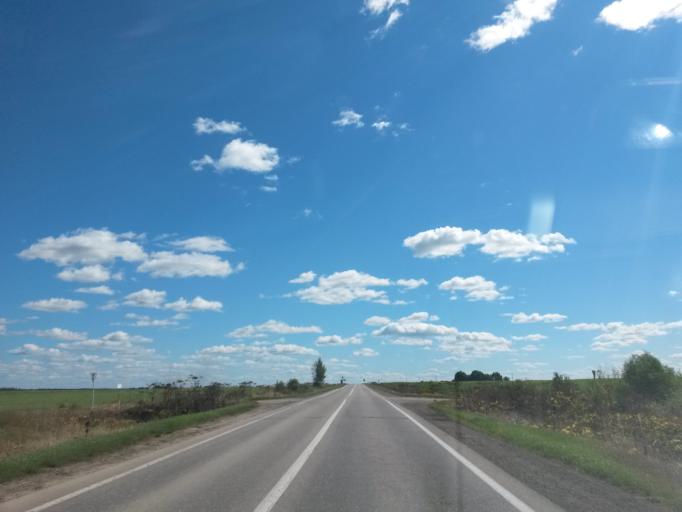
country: RU
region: Jaroslavl
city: Yaroslavl
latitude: 57.7620
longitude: 39.8644
